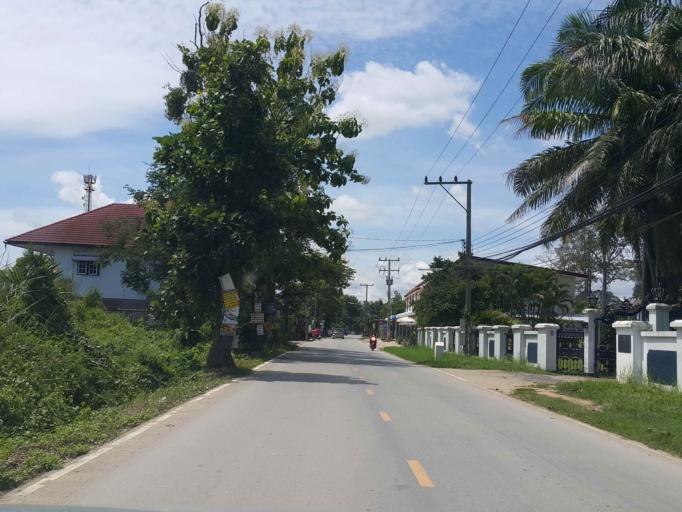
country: TH
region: Chiang Mai
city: San Sai
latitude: 18.8017
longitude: 99.0611
